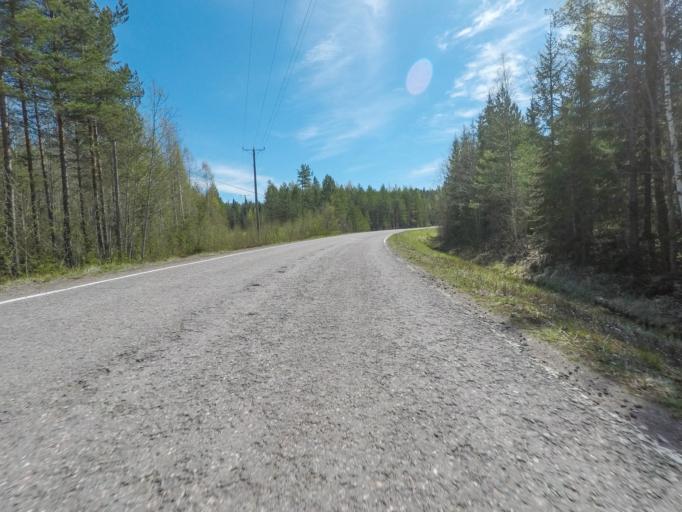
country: FI
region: Uusimaa
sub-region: Helsinki
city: Kaerkoelae
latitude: 60.6157
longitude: 23.8500
